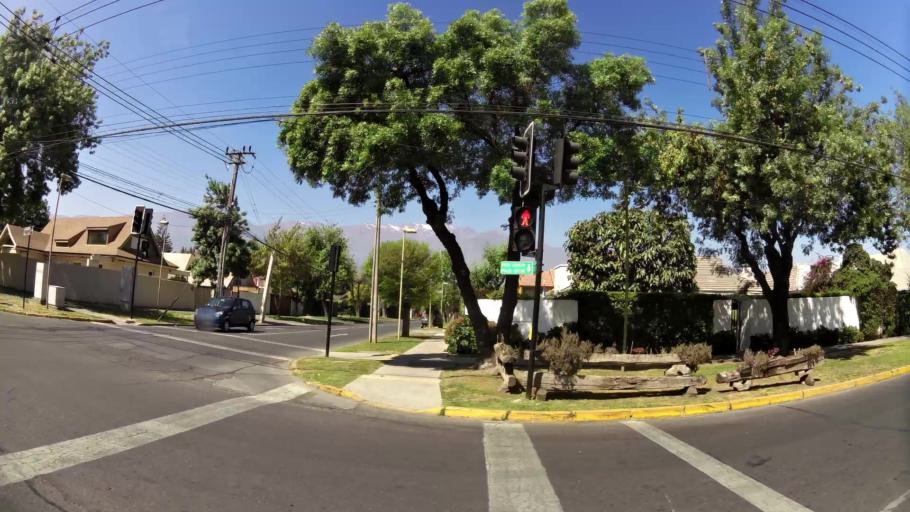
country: CL
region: Santiago Metropolitan
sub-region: Provincia de Santiago
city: Villa Presidente Frei, Nunoa, Santiago, Chile
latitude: -33.4115
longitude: -70.5461
